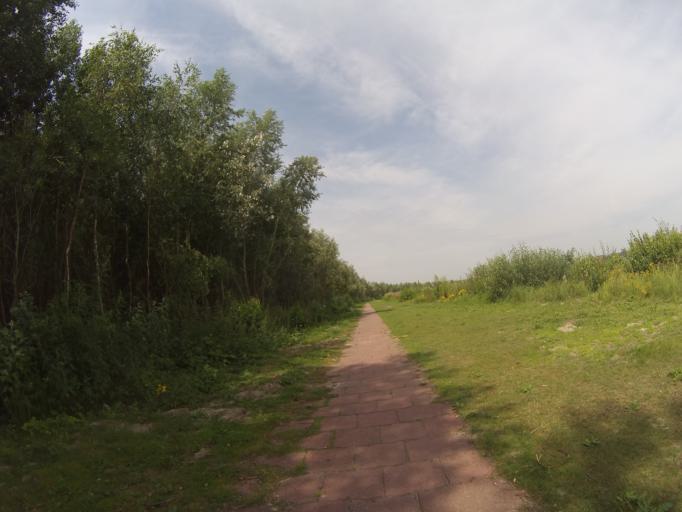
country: NL
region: Gelderland
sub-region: Gemeente Nijkerk
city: Nijkerk
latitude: 52.2646
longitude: 5.5279
